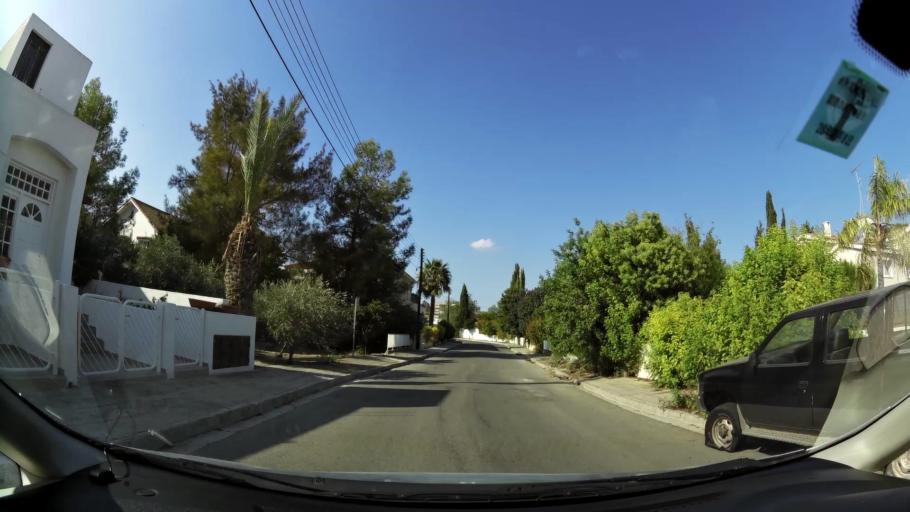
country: CY
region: Lefkosia
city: Nicosia
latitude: 35.1553
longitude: 33.3041
